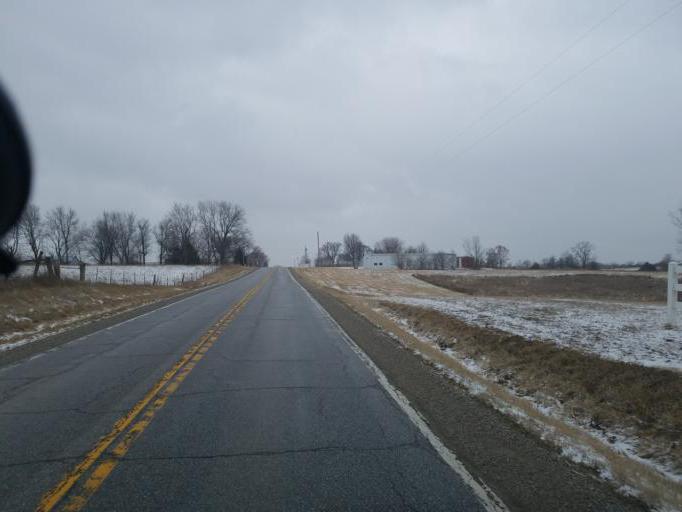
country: US
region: Missouri
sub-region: Putnam County
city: Unionville
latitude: 40.5122
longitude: -93.0093
